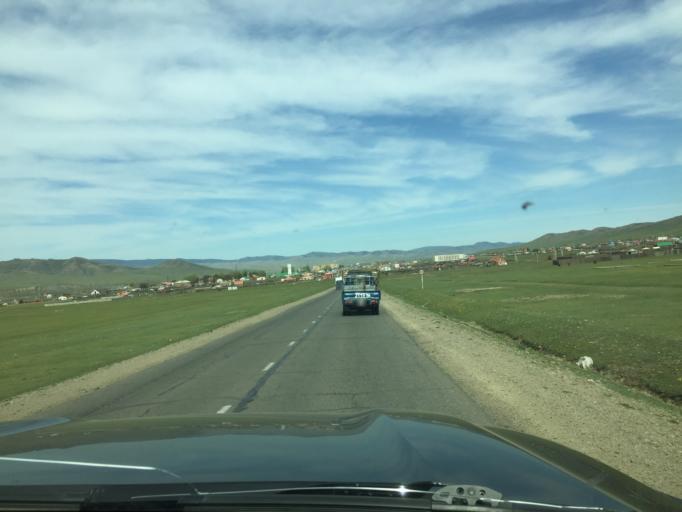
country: MN
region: Central Aimak
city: Ihsueuej
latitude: 48.2177
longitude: 106.3049
